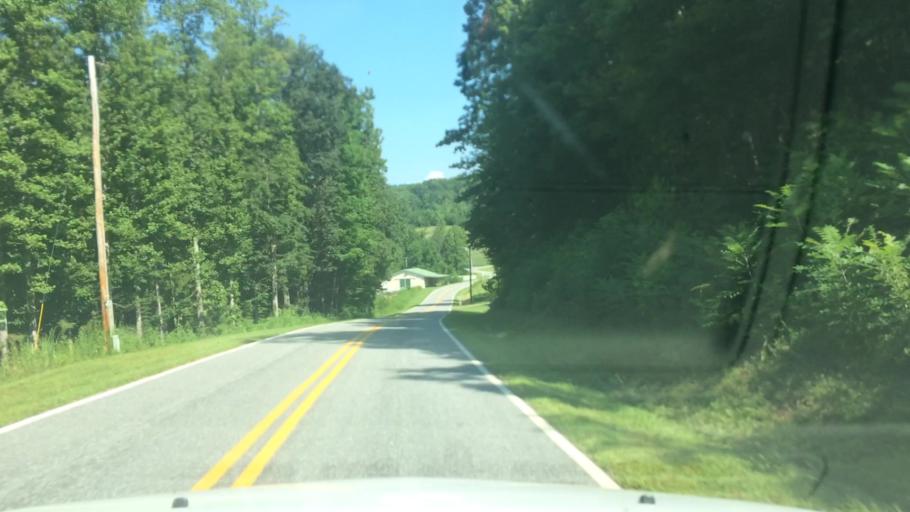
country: US
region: North Carolina
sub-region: Alexander County
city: Taylorsville
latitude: 35.9829
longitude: -81.2795
